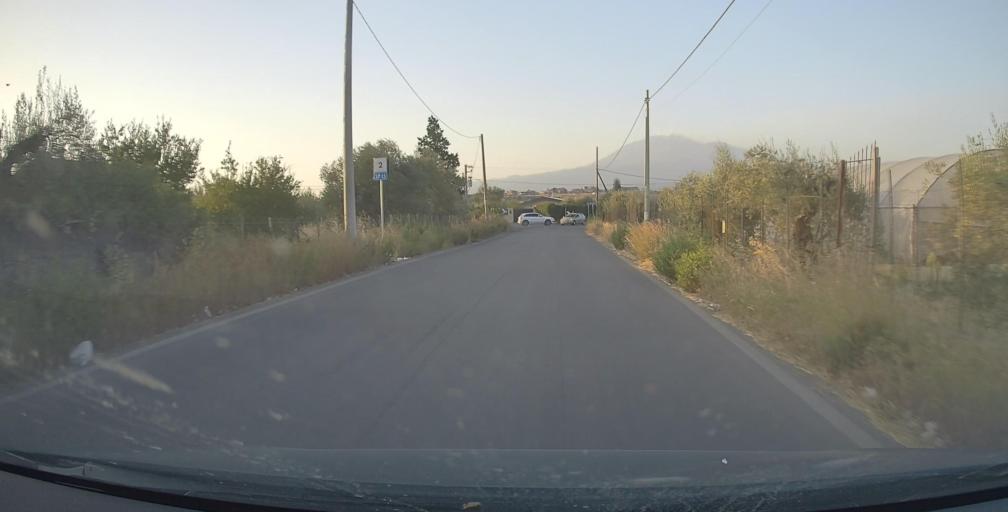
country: IT
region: Sicily
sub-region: Catania
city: Palazzolo
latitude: 37.5456
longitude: 14.9303
